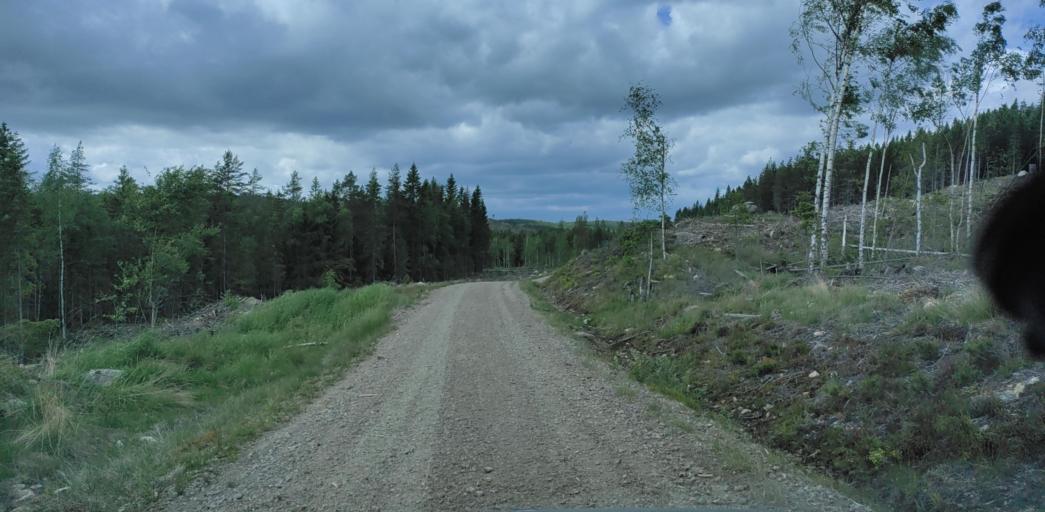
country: SE
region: Vaermland
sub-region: Munkfors Kommun
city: Munkfors
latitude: 59.9501
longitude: 13.4154
